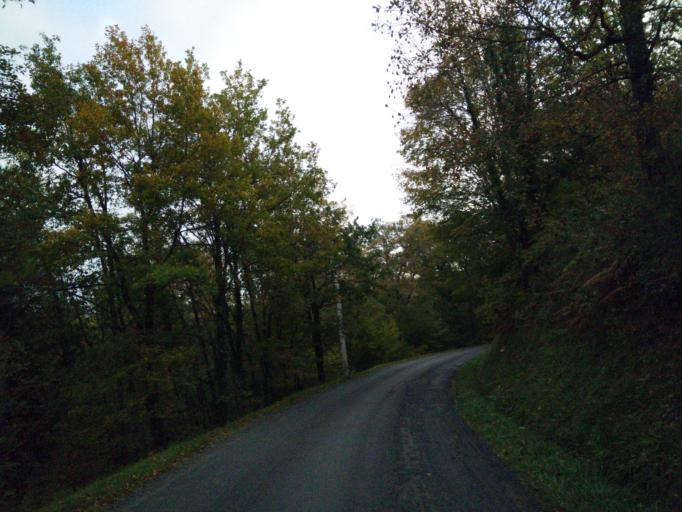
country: FR
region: Aquitaine
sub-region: Departement de la Dordogne
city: Rouffignac-Saint-Cernin-de-Reilhac
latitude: 45.0042
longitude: 0.9507
